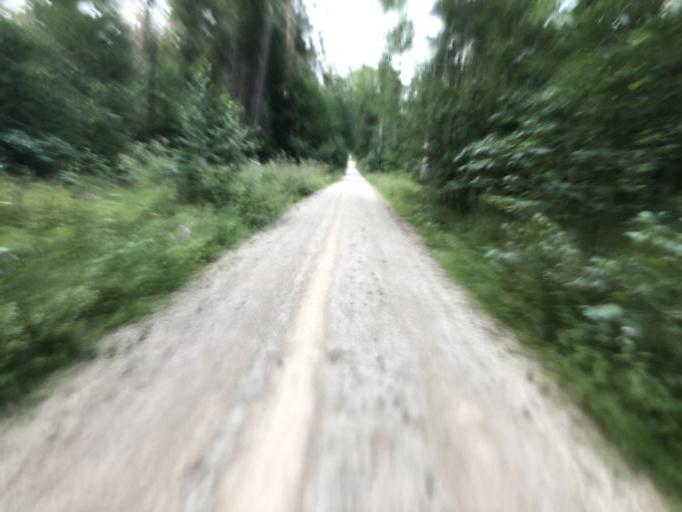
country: DE
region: Bavaria
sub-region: Regierungsbezirk Mittelfranken
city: Uttenreuth
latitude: 49.5721
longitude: 11.0759
